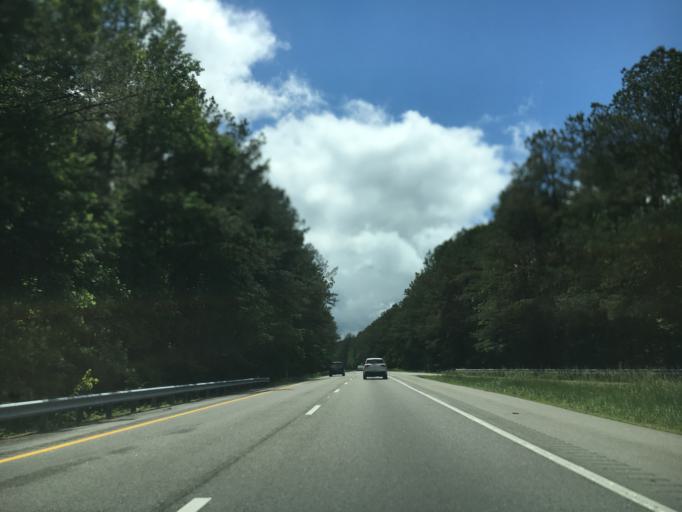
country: US
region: Virginia
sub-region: Brunswick County
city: Lawrenceville
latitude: 36.8211
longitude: -77.9624
